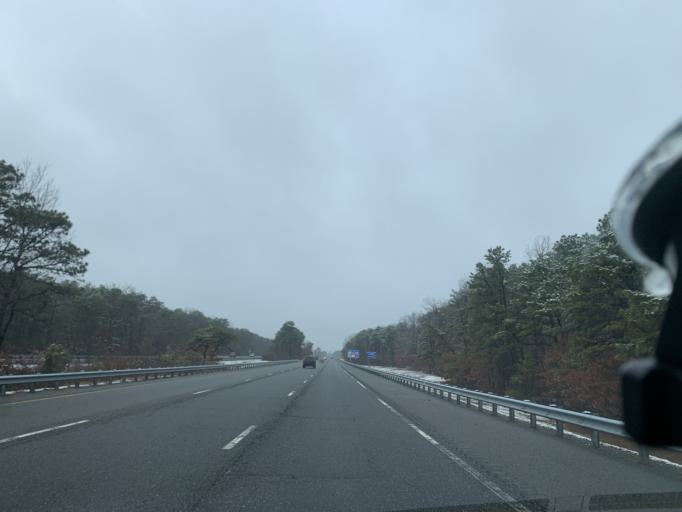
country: US
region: New Jersey
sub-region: Atlantic County
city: Pomona
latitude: 39.4378
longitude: -74.5942
